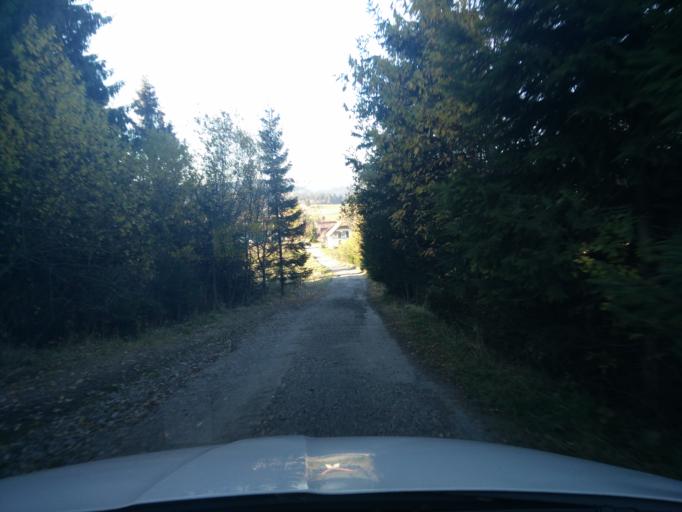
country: SK
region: Zilinsky
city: Oravska Lesna
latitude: 49.3563
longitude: 19.1532
